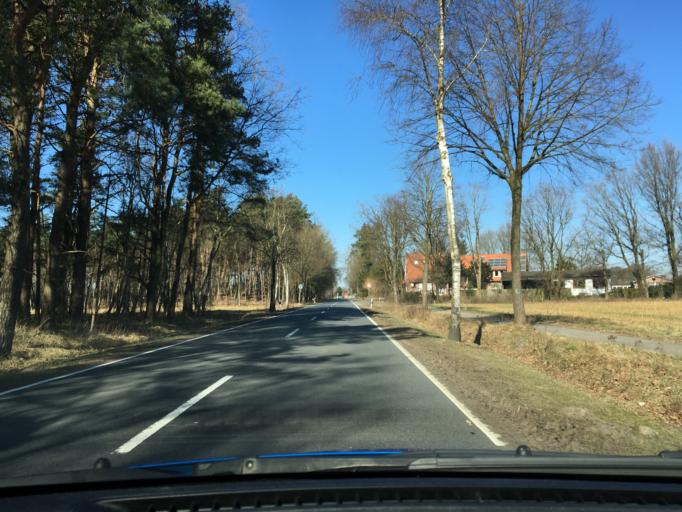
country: DE
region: Lower Saxony
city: Schneverdingen
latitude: 53.0805
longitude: 9.8089
